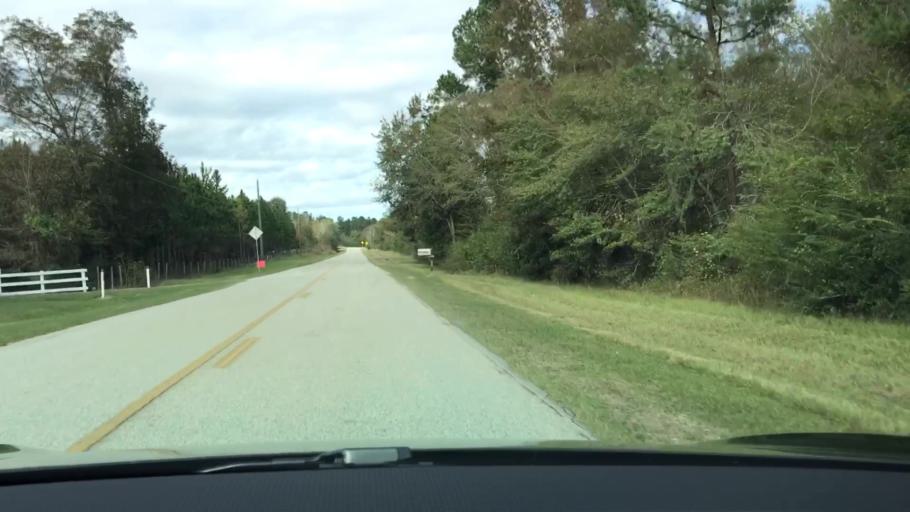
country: US
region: Georgia
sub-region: Jefferson County
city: Wadley
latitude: 32.7997
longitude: -82.3807
